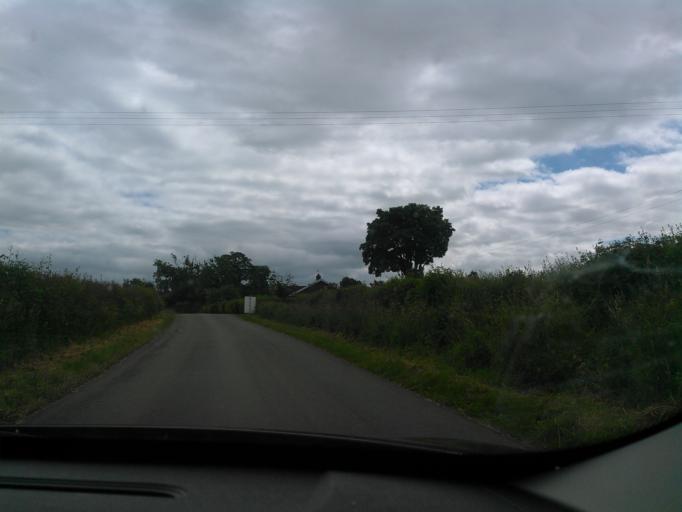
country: GB
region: England
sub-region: Shropshire
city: Whitchurch
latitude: 52.9231
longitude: -2.7277
